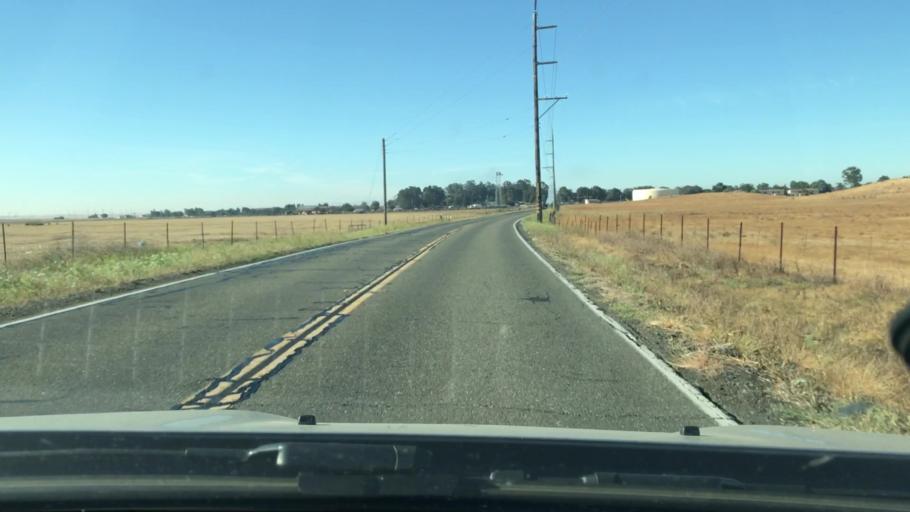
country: US
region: California
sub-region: Solano County
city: Vacaville
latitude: 38.2932
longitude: -121.9330
